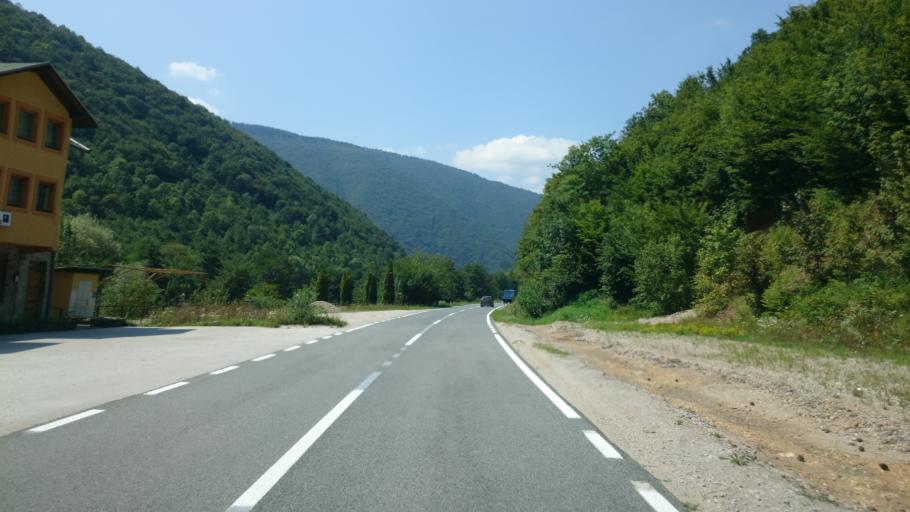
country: BA
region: Federation of Bosnia and Herzegovina
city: Donji Vakuf
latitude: 44.2075
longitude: 17.3348
